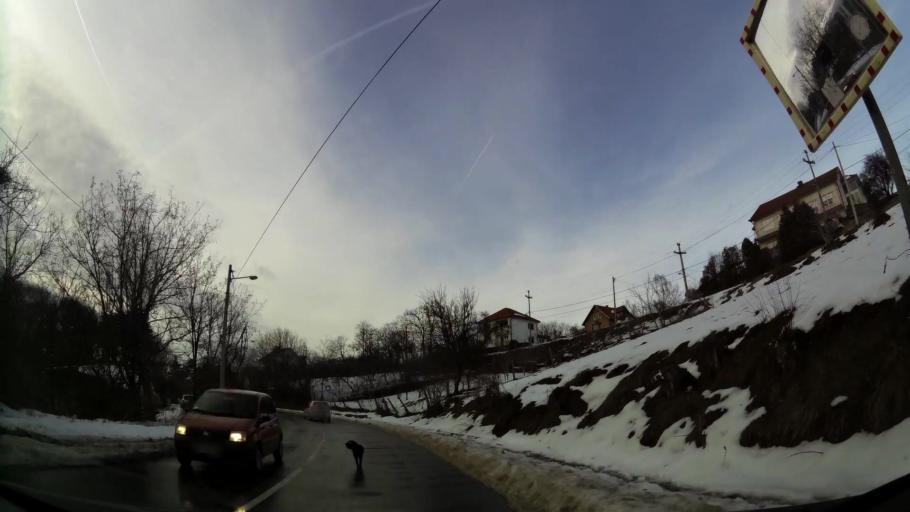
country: RS
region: Central Serbia
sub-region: Belgrade
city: Zvezdara
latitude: 44.7385
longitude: 20.5133
